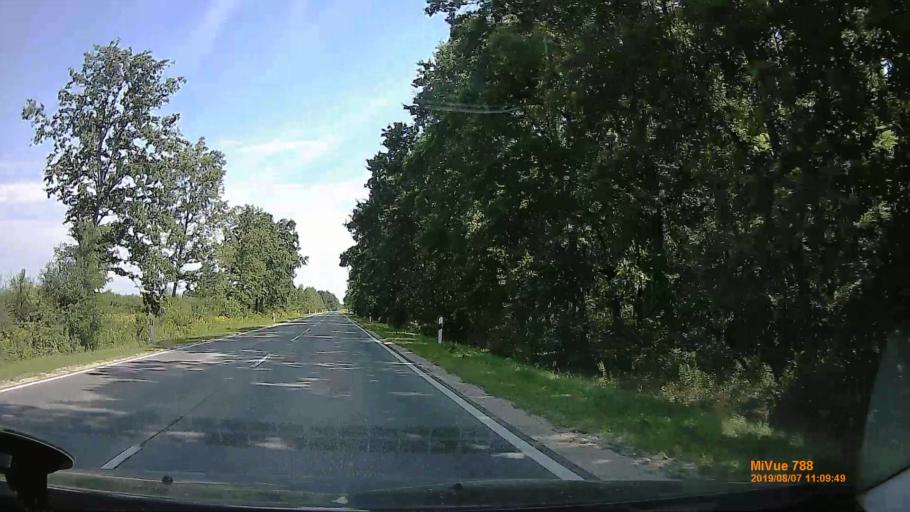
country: HU
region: Zala
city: Lenti
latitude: 46.6563
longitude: 16.4989
